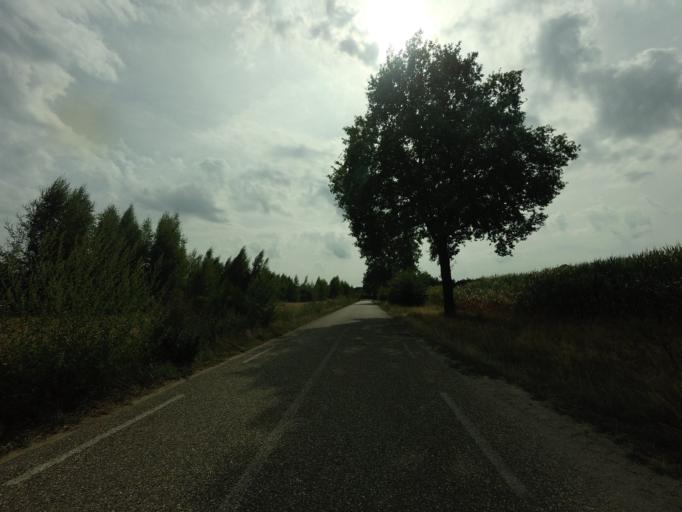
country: NL
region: North Brabant
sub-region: Gemeente Helmond
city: Helmond
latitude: 51.5100
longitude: 5.7572
